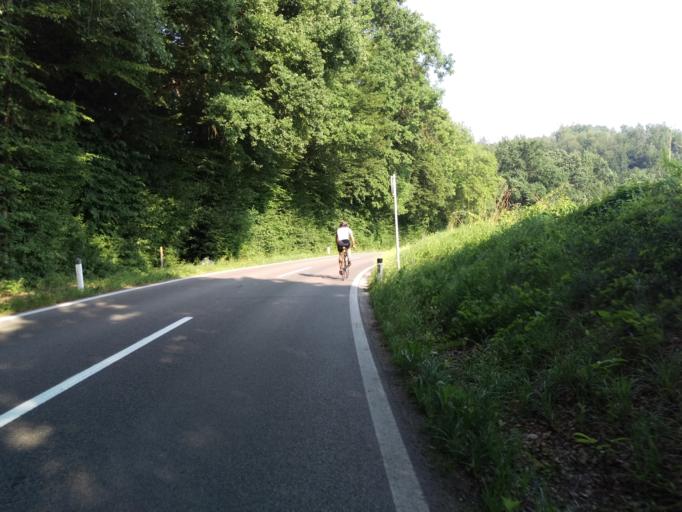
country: AT
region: Styria
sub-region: Politischer Bezirk Graz-Umgebung
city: Thal
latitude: 47.0691
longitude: 15.3652
